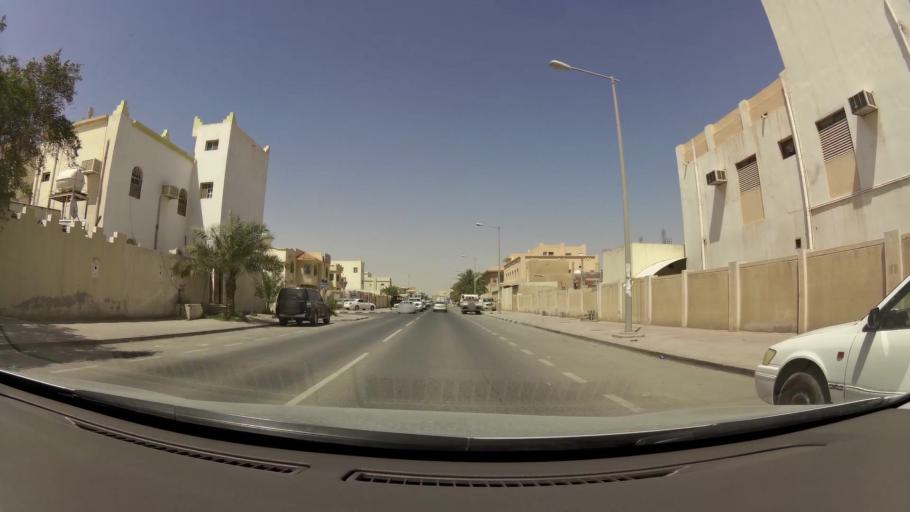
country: QA
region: Baladiyat ar Rayyan
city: Ar Rayyan
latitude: 25.2797
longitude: 51.4078
